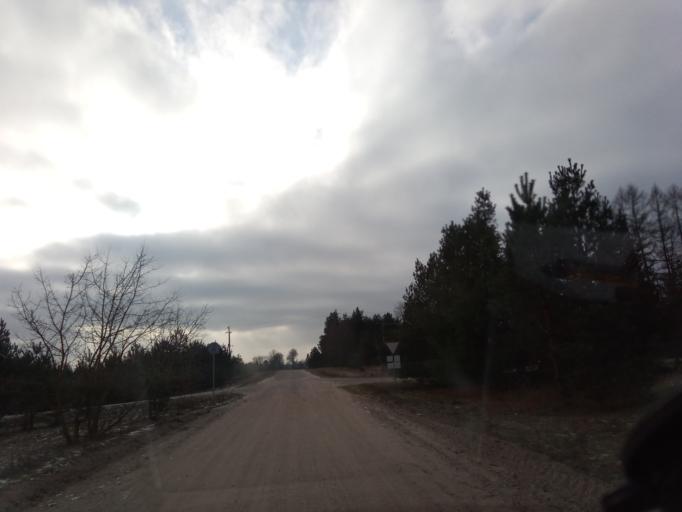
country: LT
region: Alytaus apskritis
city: Druskininkai
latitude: 53.9586
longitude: 24.3016
